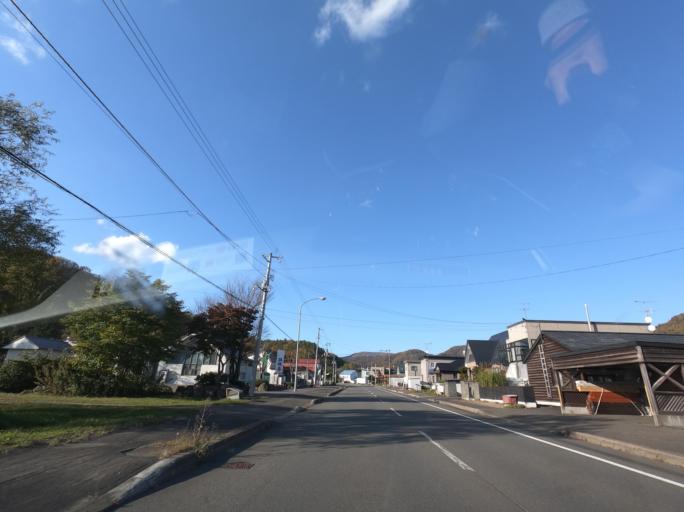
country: JP
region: Hokkaido
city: Iwamizawa
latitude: 42.9973
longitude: 142.0066
